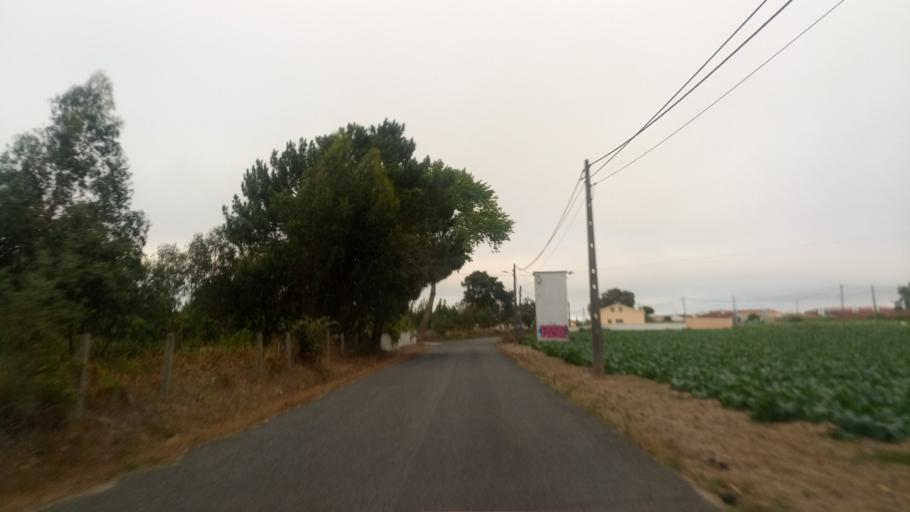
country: PT
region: Leiria
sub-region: Caldas da Rainha
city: Caldas da Rainha
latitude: 39.4206
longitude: -9.1476
